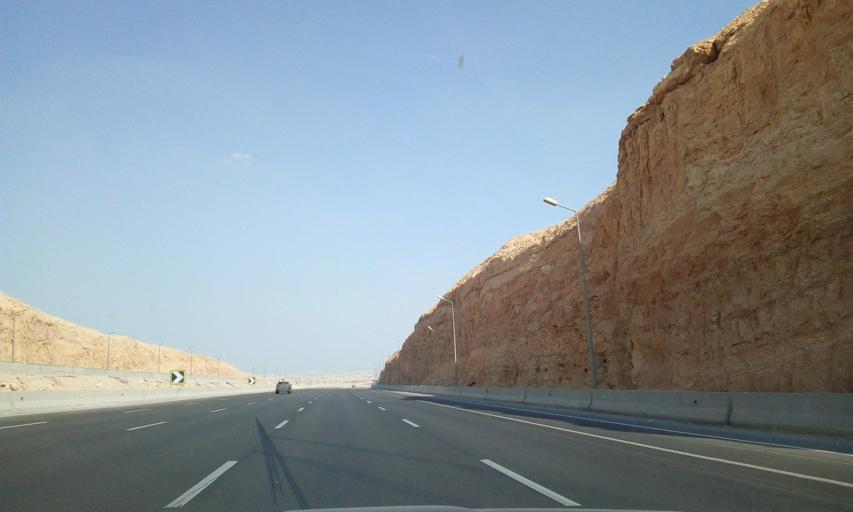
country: EG
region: As Suways
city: Ain Sukhna
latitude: 29.6826
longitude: 32.2120
